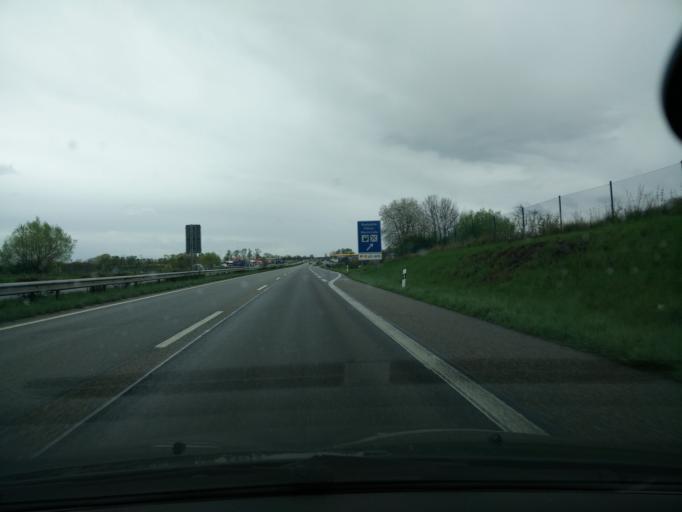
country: DE
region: Rheinland-Pfalz
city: Edesheim
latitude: 49.2741
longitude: 8.1531
